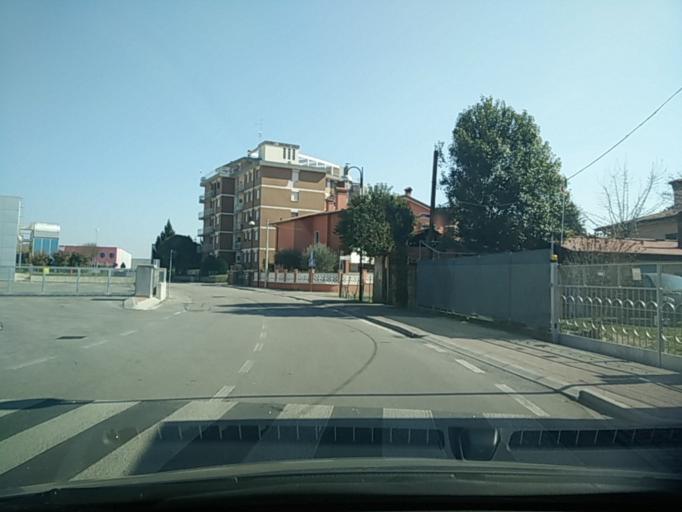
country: IT
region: Friuli Venezia Giulia
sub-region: Provincia di Pordenone
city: Pordenone
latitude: 45.9381
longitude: 12.6476
